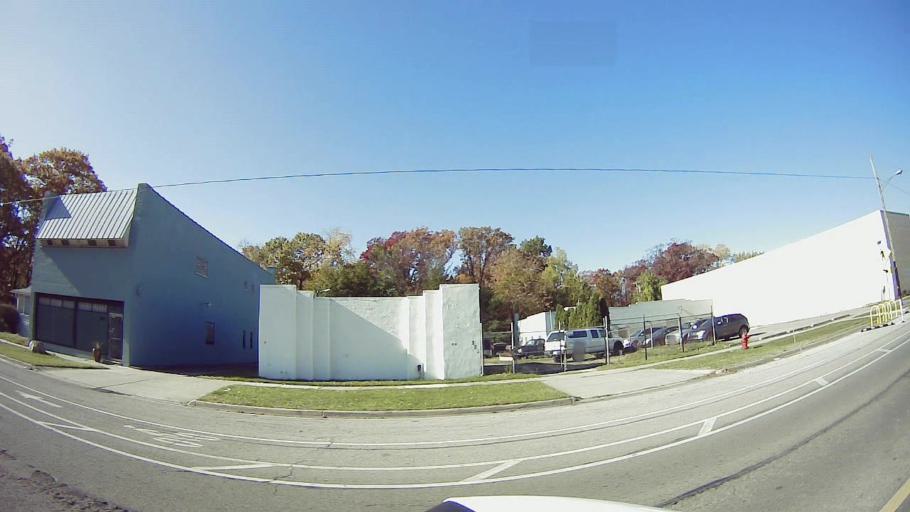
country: US
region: Michigan
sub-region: Oakland County
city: Ferndale
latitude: 42.4494
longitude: -83.1424
